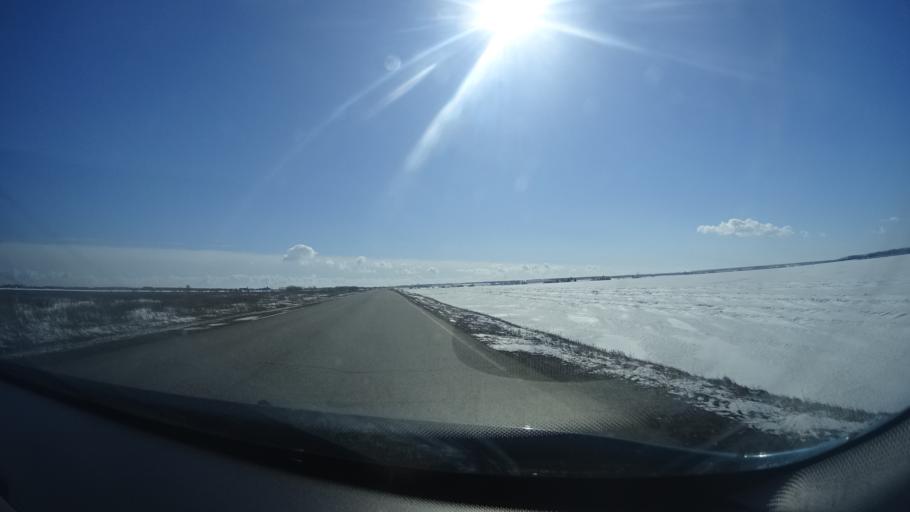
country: RU
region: Bashkortostan
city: Avdon
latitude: 54.5944
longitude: 55.8531
